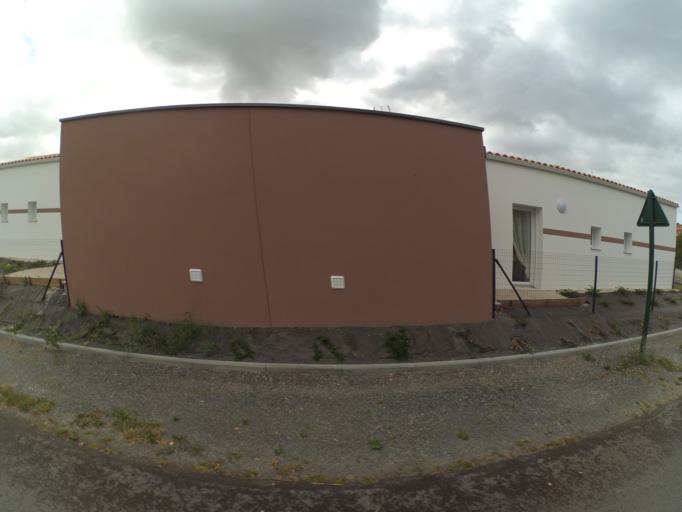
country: FR
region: Pays de la Loire
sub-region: Departement de la Vendee
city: La Bernardiere
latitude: 47.0518
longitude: -1.2662
